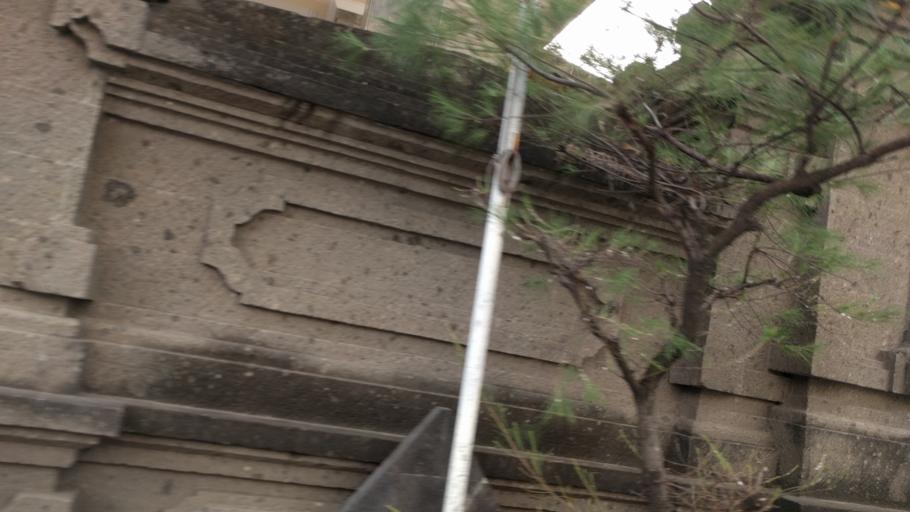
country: ID
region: Bali
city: Kuta
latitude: -8.6988
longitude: 115.1692
